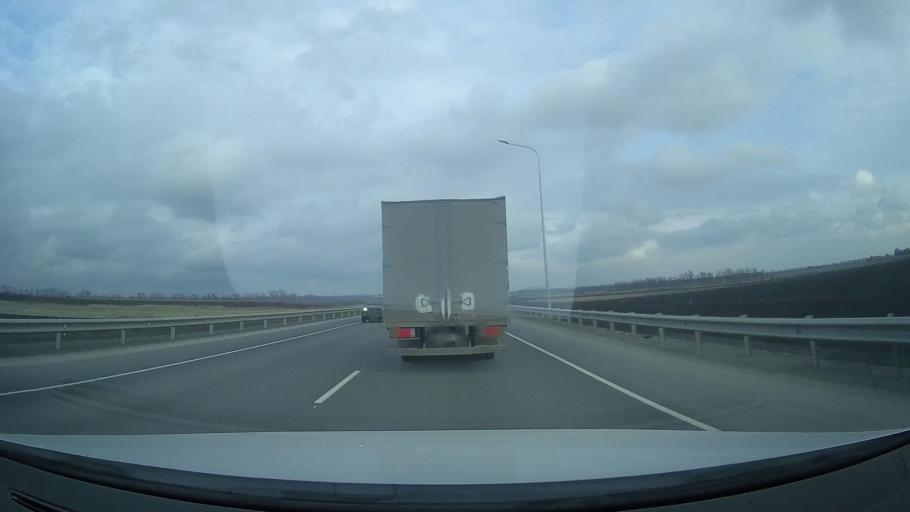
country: RU
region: Rostov
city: Grushevskaya
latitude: 47.4599
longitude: 39.8877
